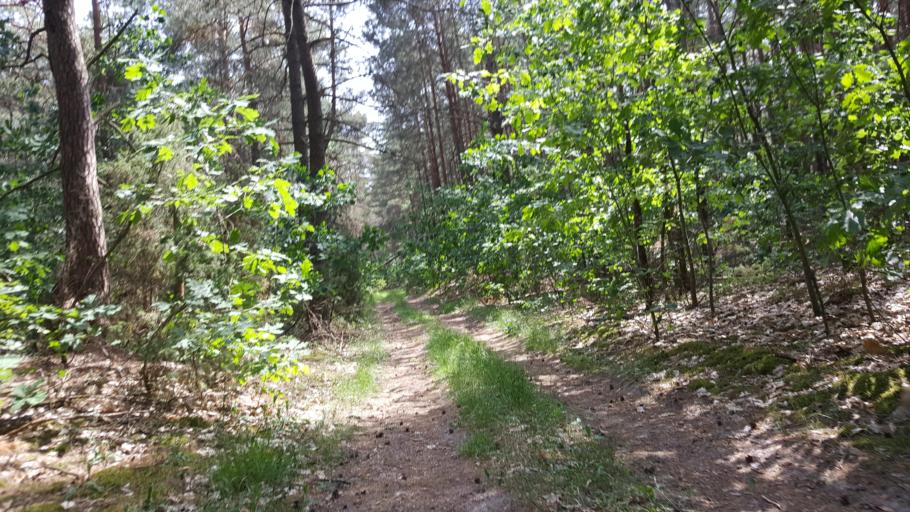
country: BY
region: Brest
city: Kamyanyuki
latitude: 52.4820
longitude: 23.8531
